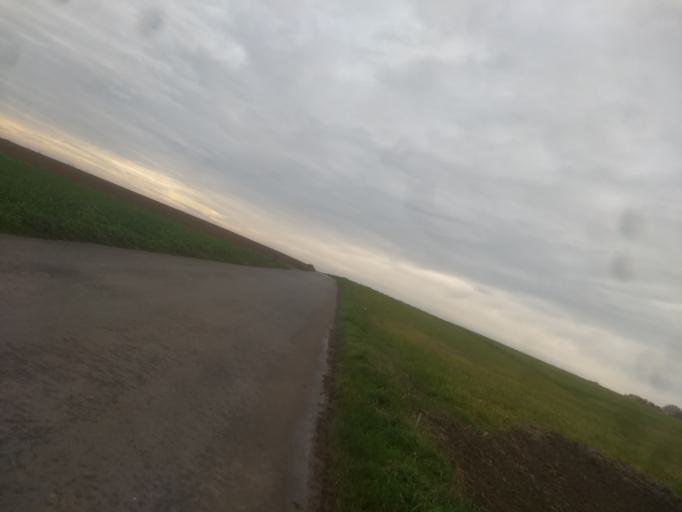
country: FR
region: Nord-Pas-de-Calais
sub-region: Departement du Pas-de-Calais
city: Dainville
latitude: 50.2553
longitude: 2.7202
